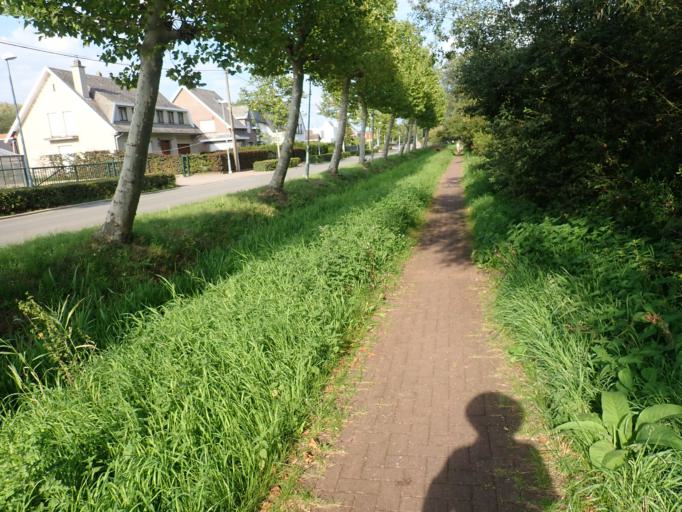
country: BE
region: Flanders
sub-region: Provincie Antwerpen
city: Puurs
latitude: 51.0805
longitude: 4.3097
